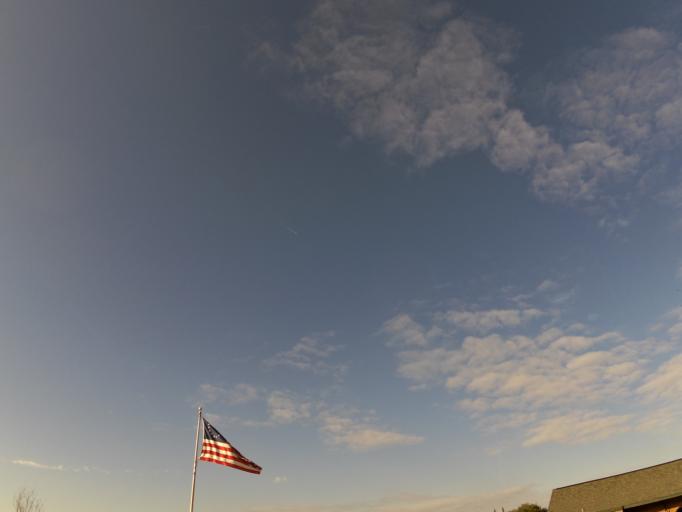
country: US
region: Georgia
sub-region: Chatham County
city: Savannah
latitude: 32.0756
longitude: -81.1005
